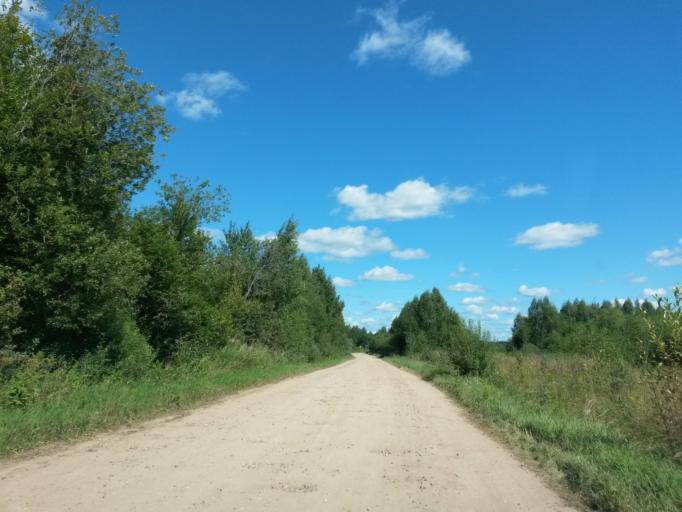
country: RU
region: Jaroslavl
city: Tutayev
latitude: 57.9474
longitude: 39.4554
